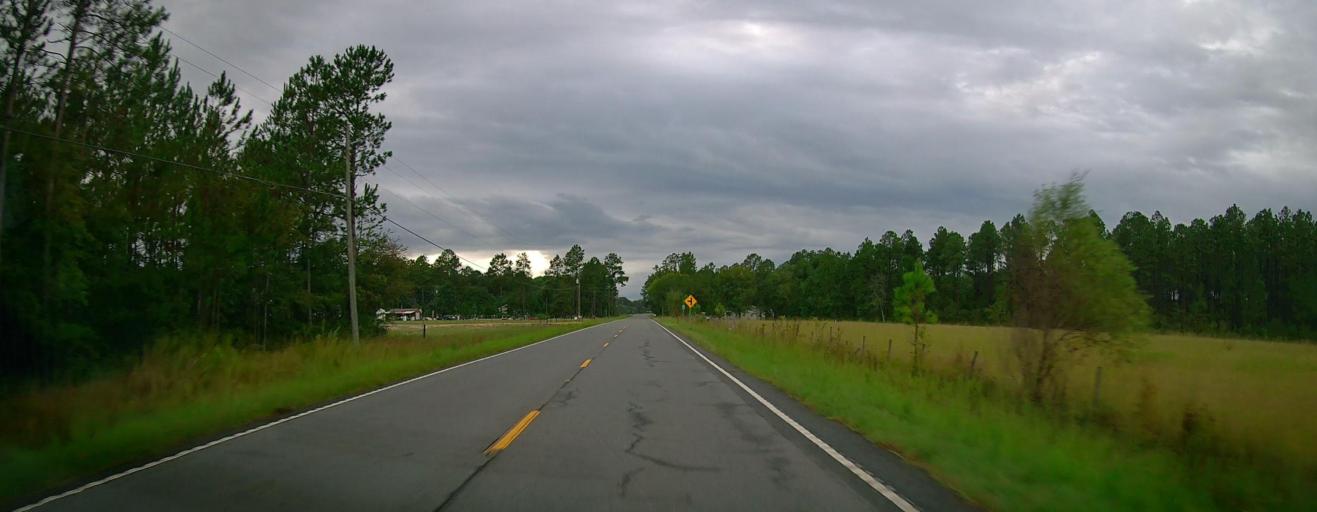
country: US
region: Georgia
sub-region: Ware County
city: Deenwood
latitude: 31.2863
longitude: -82.4373
